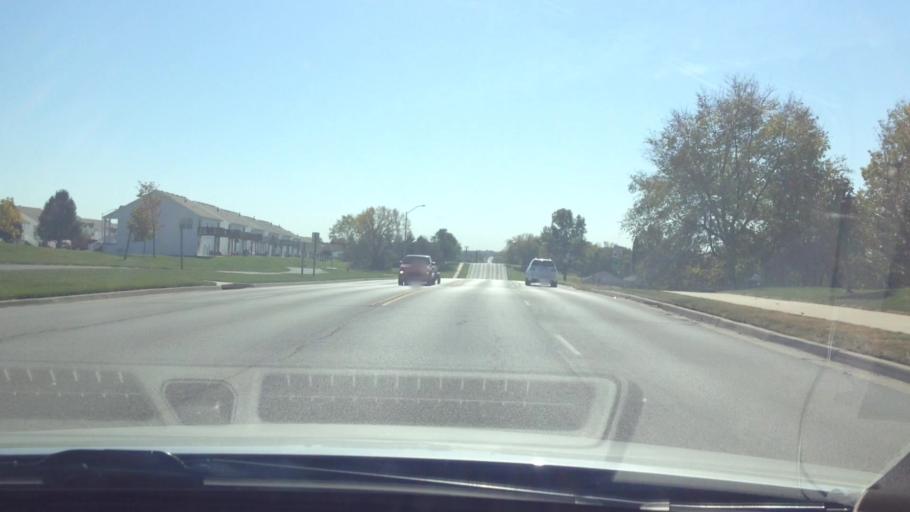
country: US
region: Missouri
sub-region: Platte County
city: Platte City
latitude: 39.3472
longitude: -94.7610
